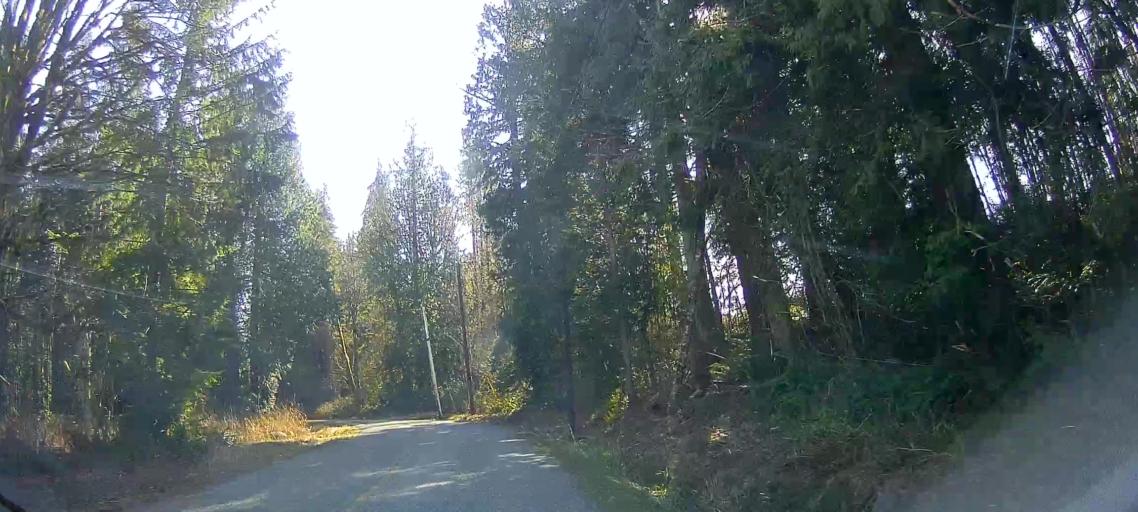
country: US
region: Washington
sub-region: Whatcom County
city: Sudden Valley
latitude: 48.6183
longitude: -122.3691
